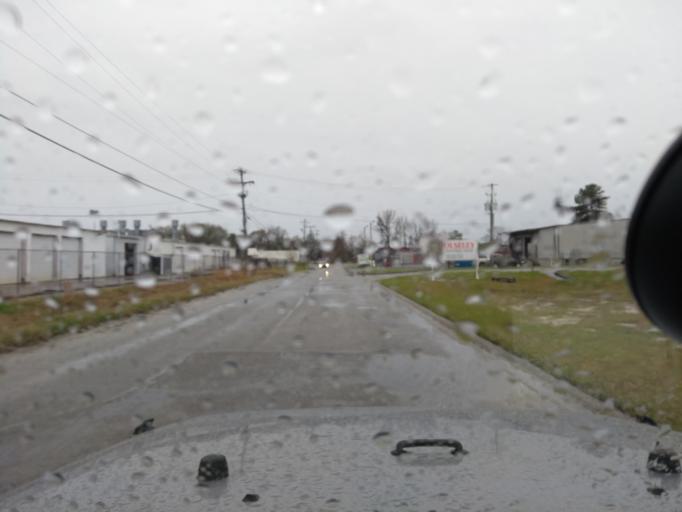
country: US
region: Georgia
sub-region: Chatham County
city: Garden City
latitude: 32.0882
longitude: -81.1599
